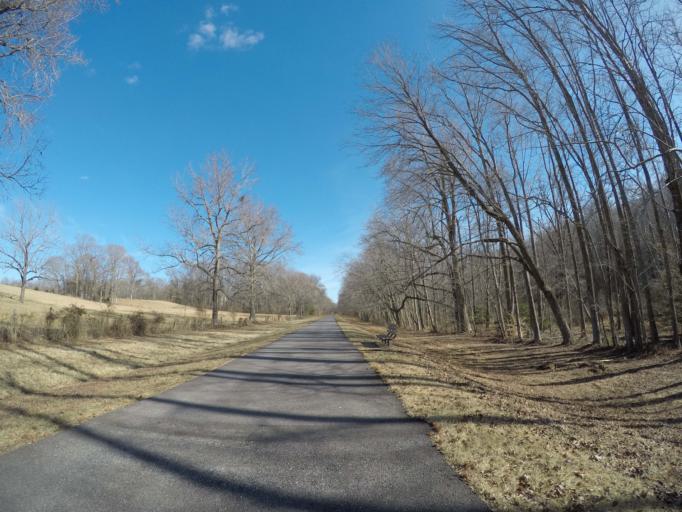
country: US
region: Maryland
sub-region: Charles County
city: Bennsville
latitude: 38.5961
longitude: -76.9977
